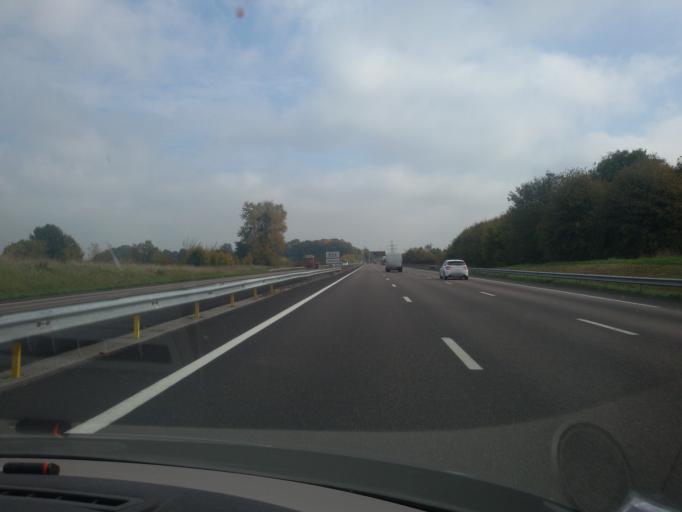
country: FR
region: Haute-Normandie
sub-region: Departement de l'Eure
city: Saint-Ouen-de-Thouberville
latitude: 49.3502
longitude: 0.8967
